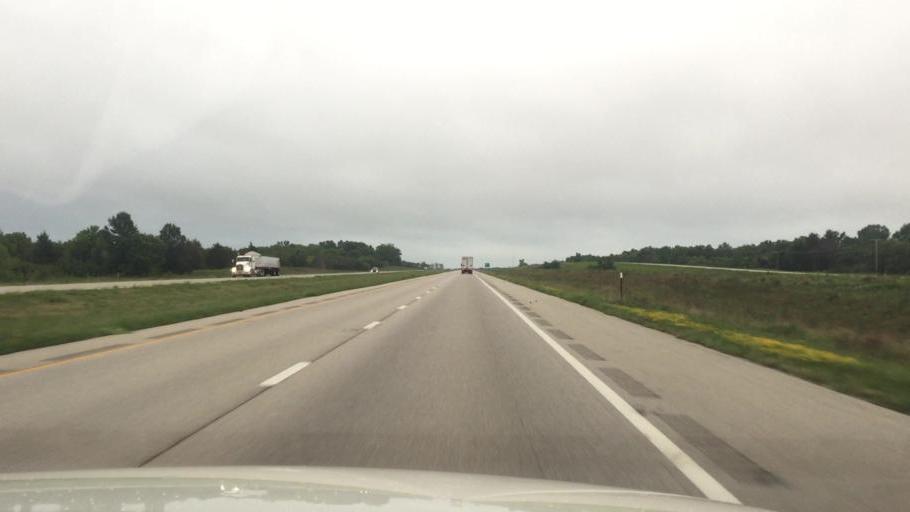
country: US
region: Kansas
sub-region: Montgomery County
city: Coffeyville
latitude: 37.0632
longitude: -95.5831
